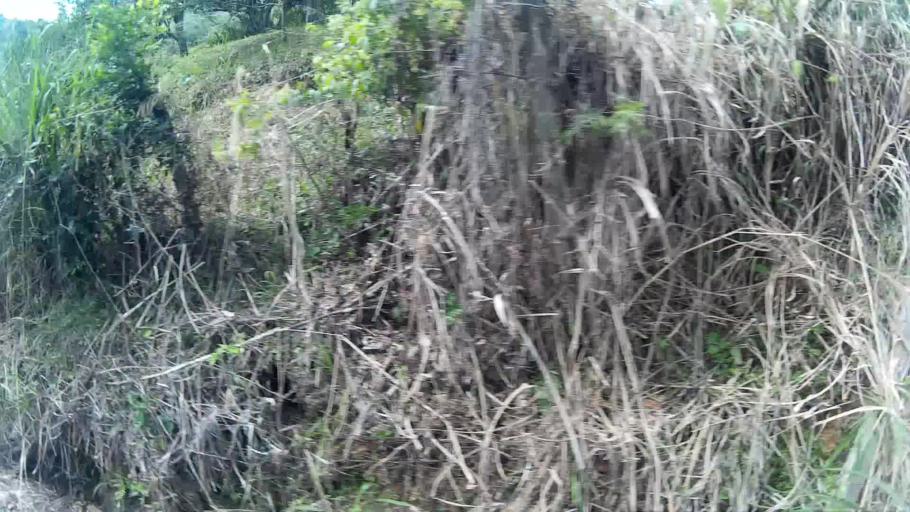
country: CO
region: Risaralda
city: La Virginia
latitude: 4.9403
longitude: -75.8391
